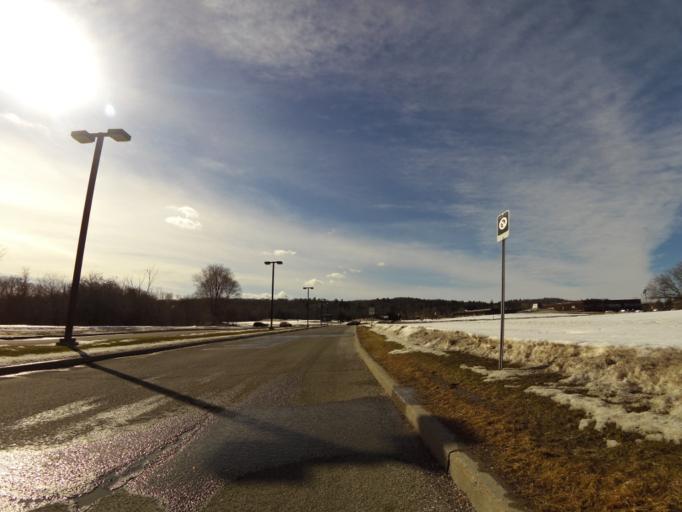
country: CA
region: Quebec
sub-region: Outaouais
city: Gatineau
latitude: 45.4503
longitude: -75.7581
